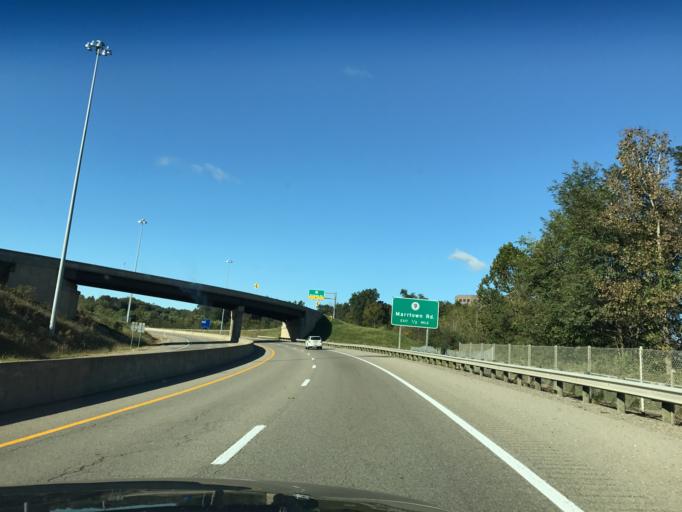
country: US
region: Ohio
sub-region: Washington County
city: Belpre
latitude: 39.2639
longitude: -81.5714
